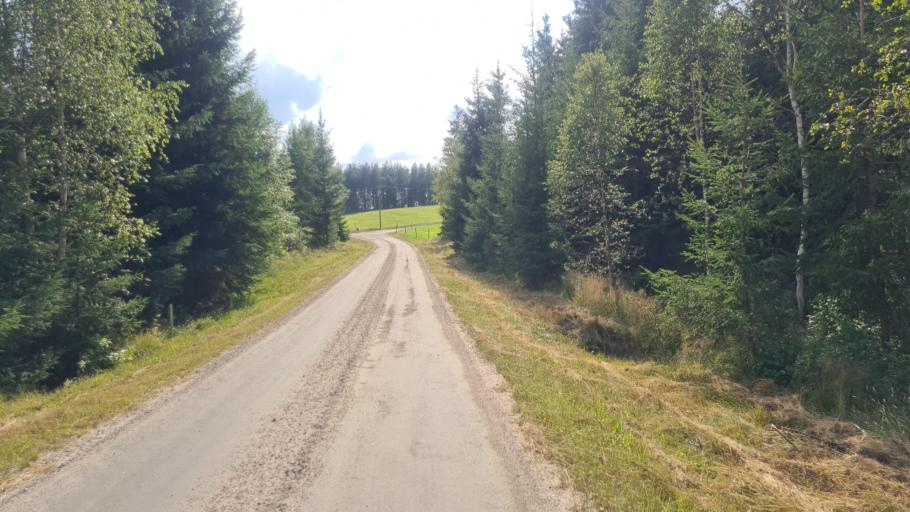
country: SE
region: Kronoberg
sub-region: Ljungby Kommun
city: Ljungby
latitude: 56.7216
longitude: 13.8826
